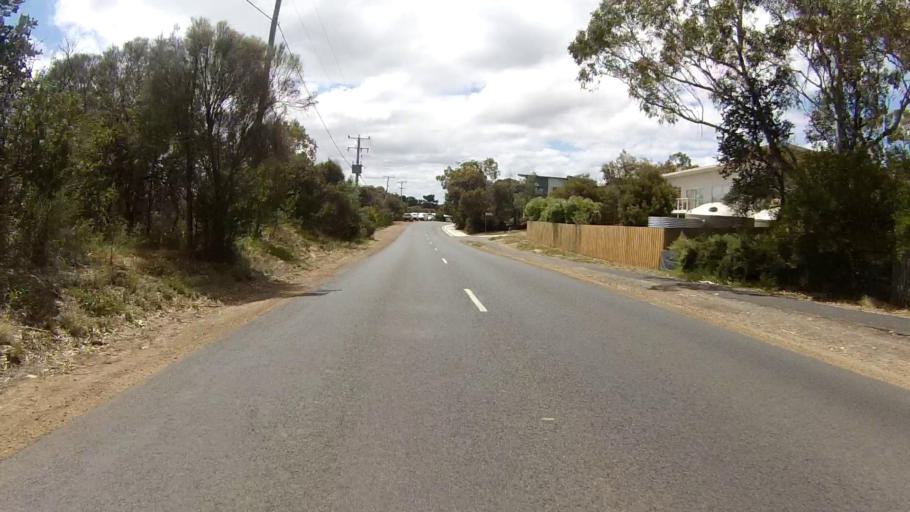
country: AU
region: Tasmania
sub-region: Sorell
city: Sorell
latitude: -42.8638
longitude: 147.6118
